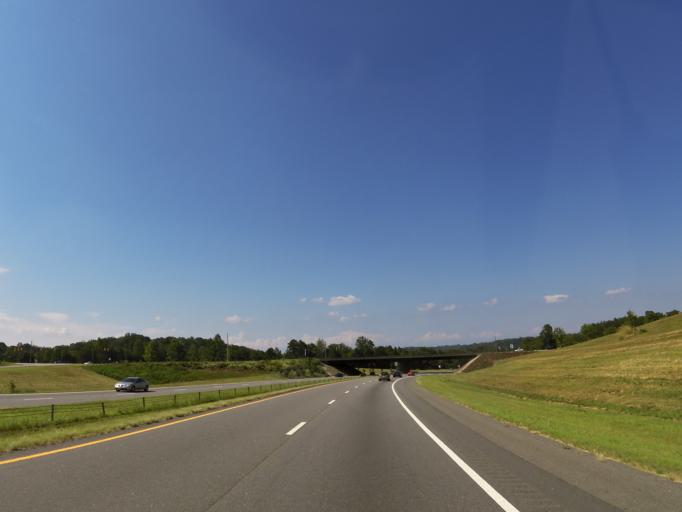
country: US
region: North Carolina
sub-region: Catawba County
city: Mountain View
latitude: 35.6922
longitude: -81.3519
